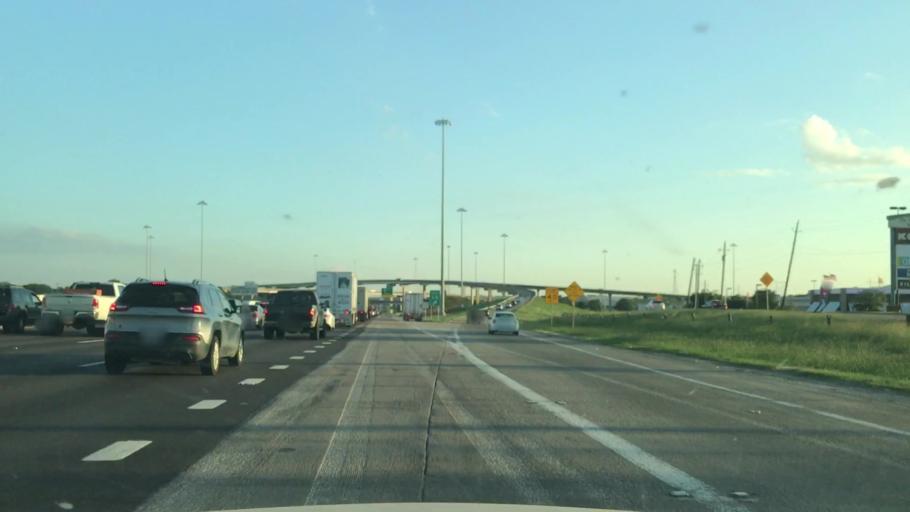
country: US
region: Texas
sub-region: Dallas County
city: Mesquite
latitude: 32.7980
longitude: -96.6261
